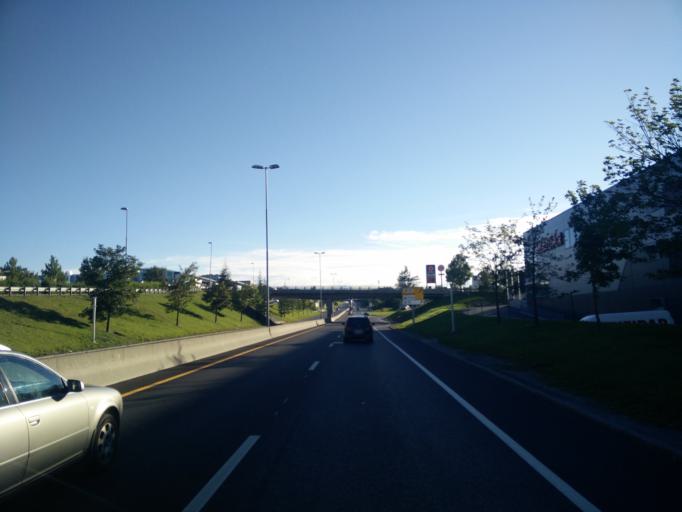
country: NO
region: Sor-Trondelag
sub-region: Trondheim
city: Trondheim
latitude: 63.4209
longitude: 10.4652
